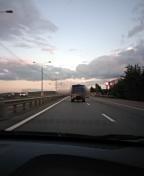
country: RU
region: Moskovskaya
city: Zhukovskiy
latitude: 55.5214
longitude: 38.1215
